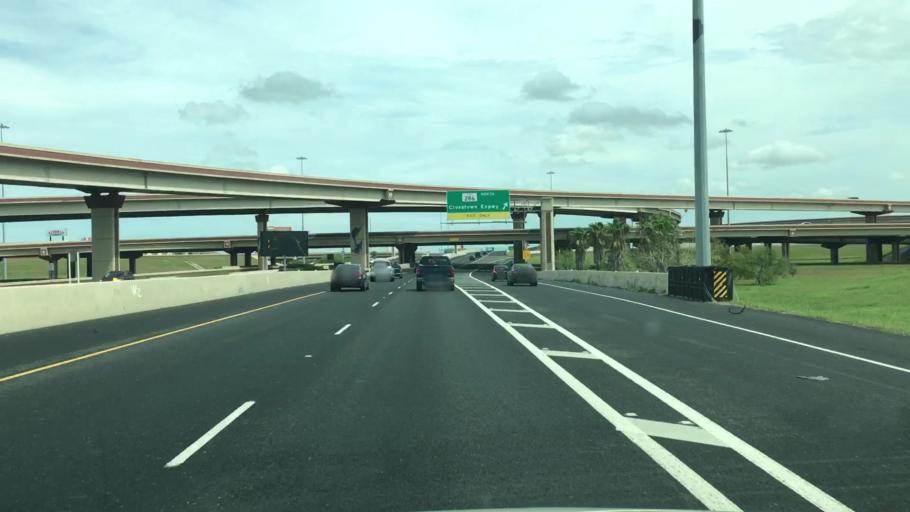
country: US
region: Texas
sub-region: Nueces County
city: Corpus Christi
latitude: 27.7381
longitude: -97.4324
